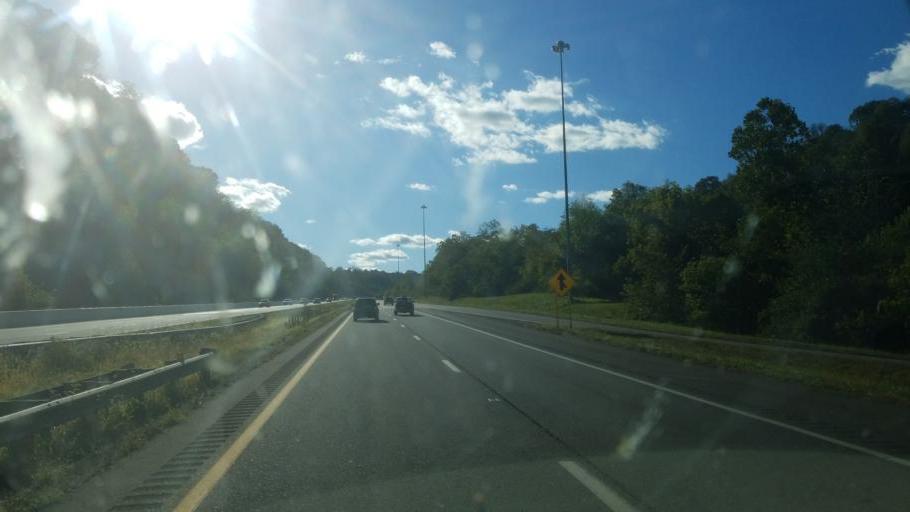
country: US
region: Ohio
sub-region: Belmont County
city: Bridgeport
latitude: 40.0484
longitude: -80.7401
